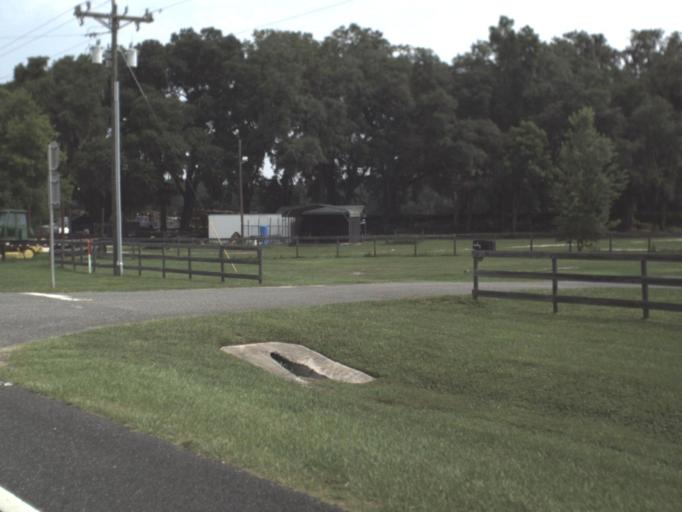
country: US
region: Florida
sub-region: Levy County
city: Williston
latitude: 29.3801
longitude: -82.4217
